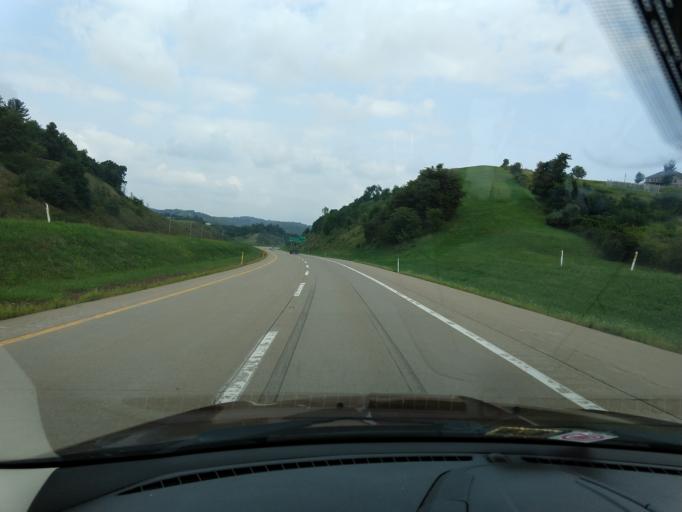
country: US
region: Pennsylvania
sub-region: Washington County
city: Gastonville
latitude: 40.2433
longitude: -79.9799
